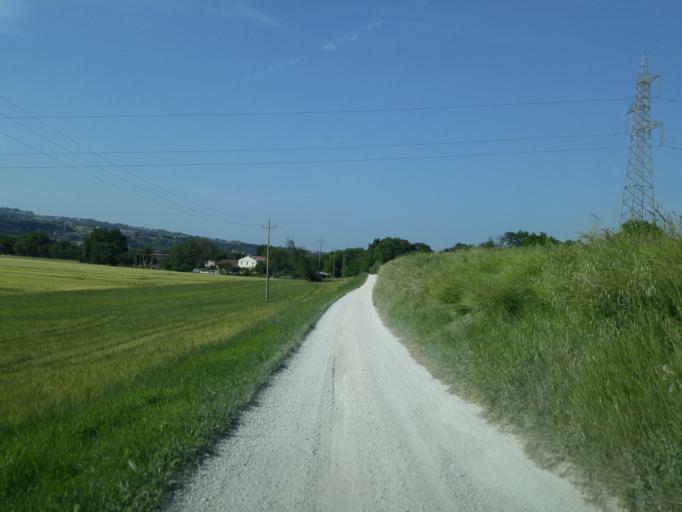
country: IT
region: The Marches
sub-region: Provincia di Pesaro e Urbino
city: Tavernelle
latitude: 43.7228
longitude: 12.8993
